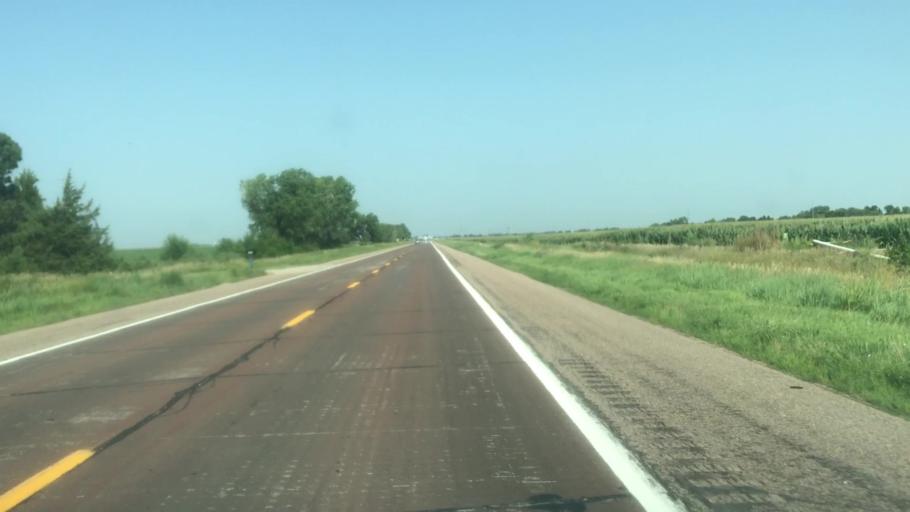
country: US
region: Nebraska
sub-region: Hall County
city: Grand Island
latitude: 40.9712
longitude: -98.5049
